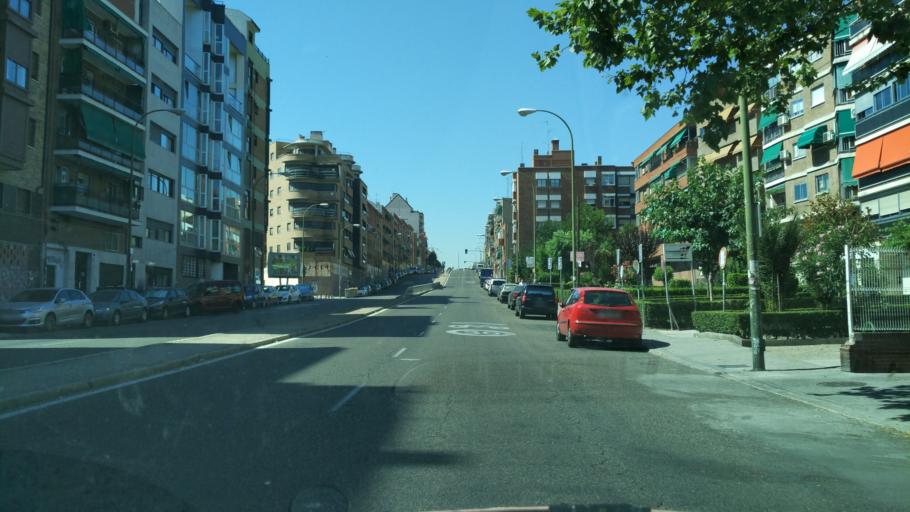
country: ES
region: Madrid
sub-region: Provincia de Madrid
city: Tetuan de las Victorias
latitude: 40.4610
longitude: -3.7092
